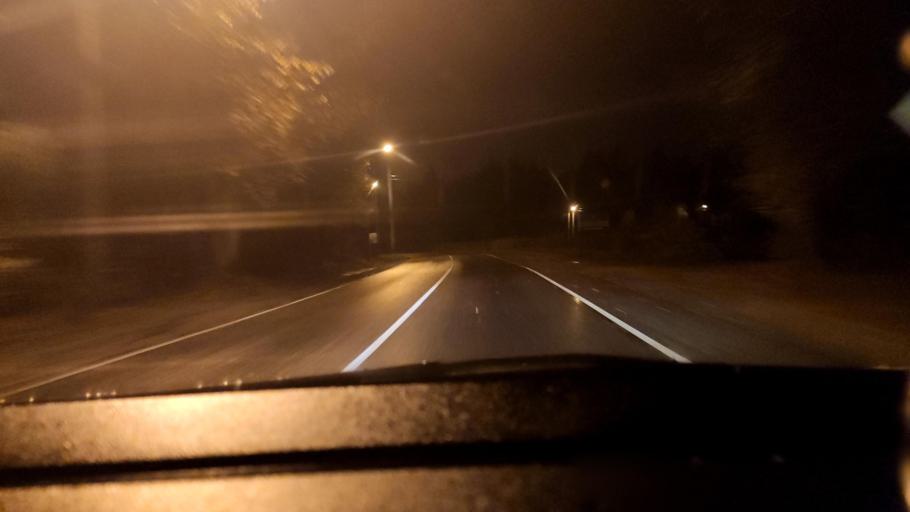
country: RU
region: Voronezj
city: Pridonskoy
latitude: 51.6340
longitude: 39.0832
